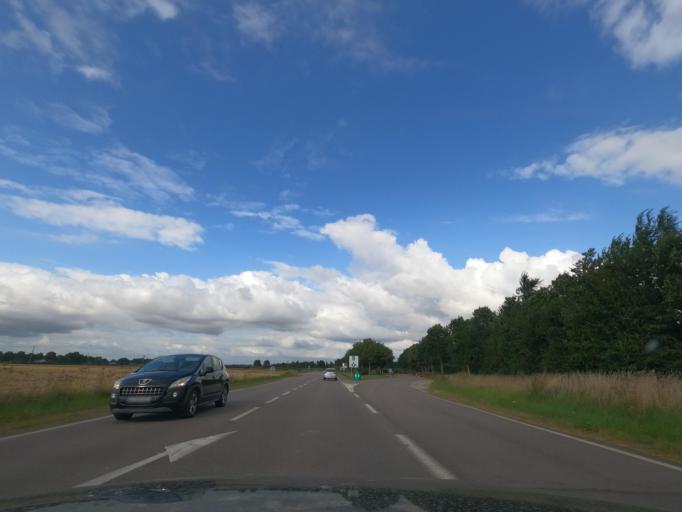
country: FR
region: Haute-Normandie
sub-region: Departement de l'Eure
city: Broglie
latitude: 48.9948
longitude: 0.5072
